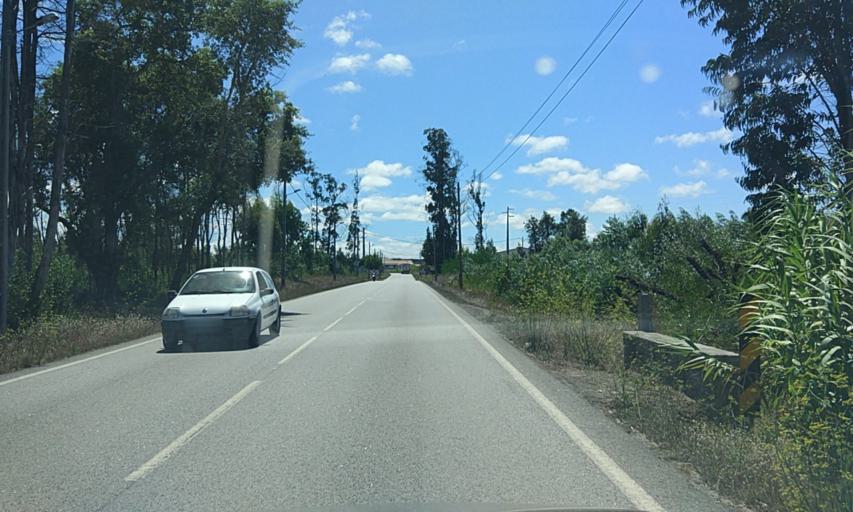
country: PT
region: Coimbra
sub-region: Mira
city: Mira
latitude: 40.4053
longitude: -8.7355
